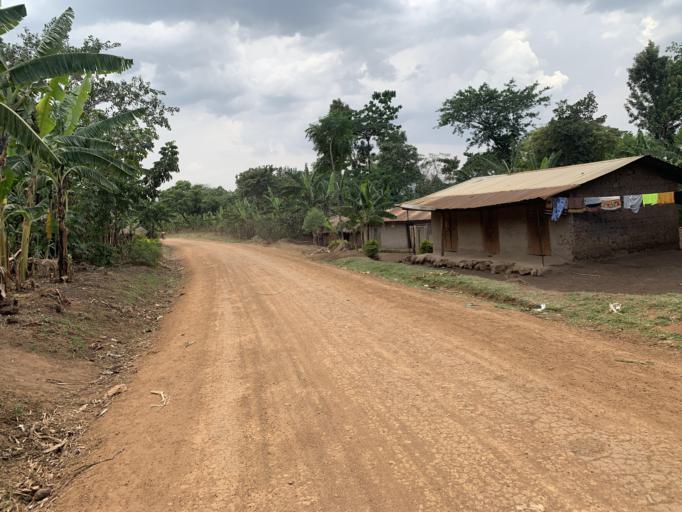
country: UG
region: Eastern Region
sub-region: Sironko District
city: Sironko
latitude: 1.2543
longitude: 34.2916
